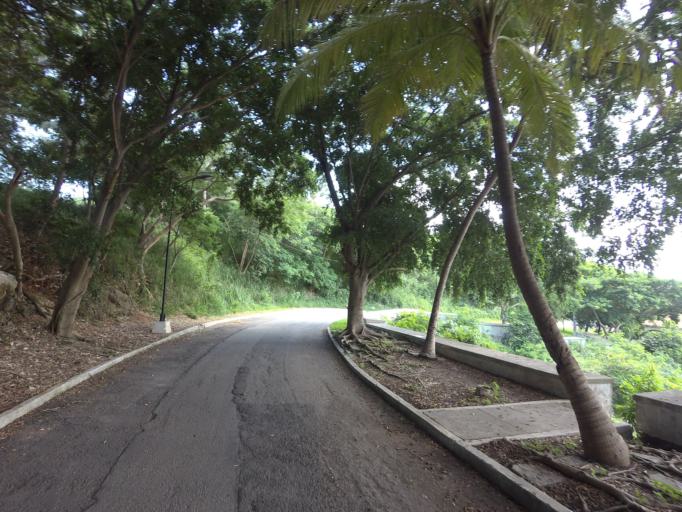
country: CU
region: La Habana
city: Centro Habana
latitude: 23.1493
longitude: -82.3532
